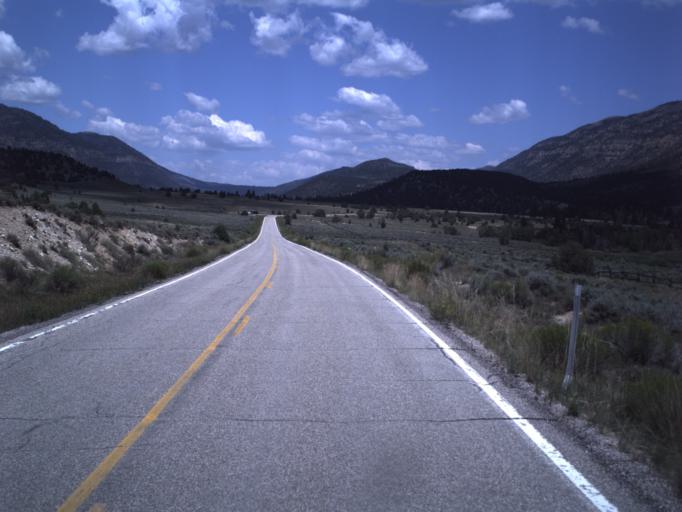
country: US
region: Utah
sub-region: Emery County
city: Orangeville
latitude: 39.3155
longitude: -111.2832
